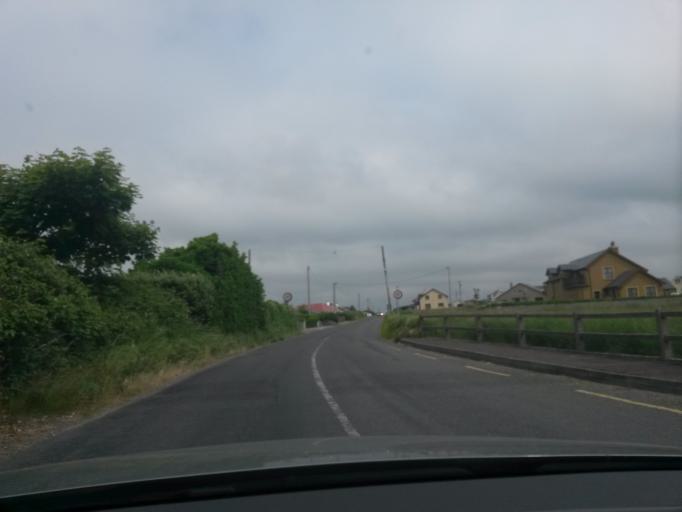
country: IE
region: Munster
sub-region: Ciarrai
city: Ballybunnion
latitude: 52.5250
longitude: -9.6704
